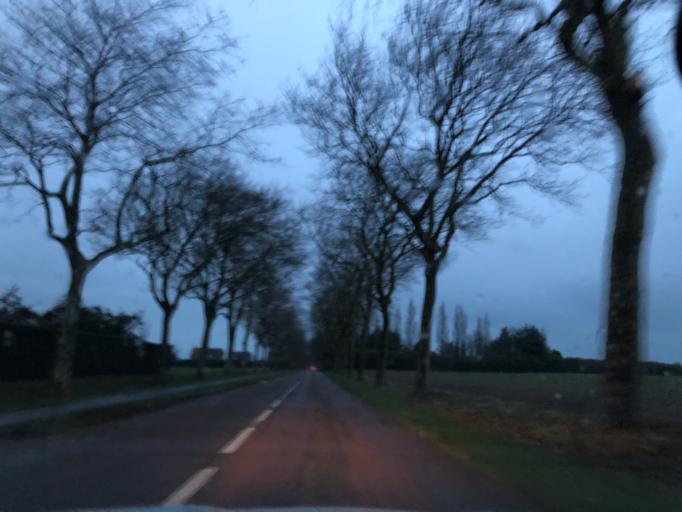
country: FR
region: Lower Normandy
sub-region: Departement du Calvados
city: Mathieu
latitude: 49.2613
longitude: -0.3749
